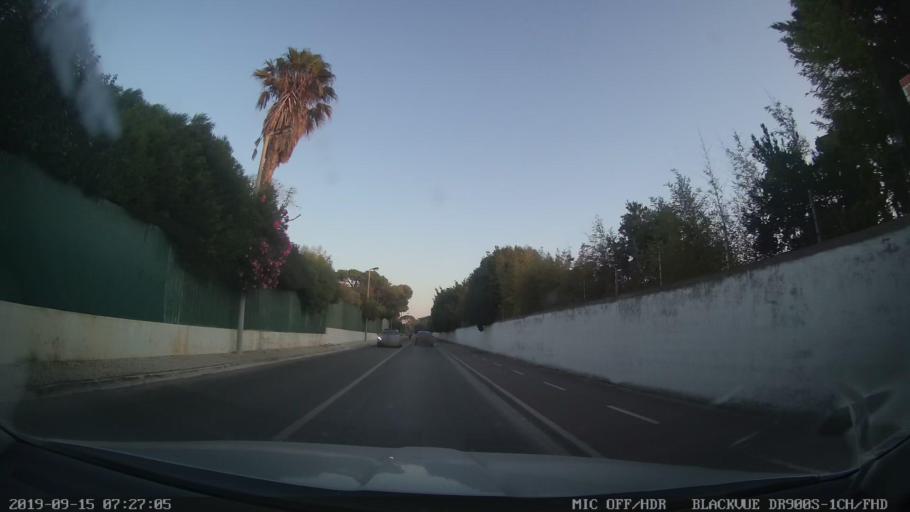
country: PT
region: Lisbon
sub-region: Cascais
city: Cascais
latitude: 38.7199
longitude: -9.4653
